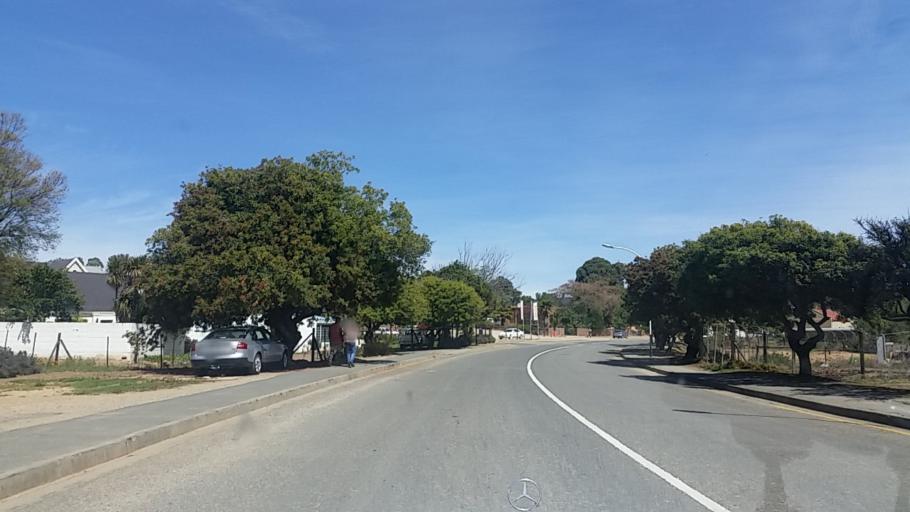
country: ZA
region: Western Cape
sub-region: Eden District Municipality
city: Knysna
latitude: -33.6589
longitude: 23.1228
